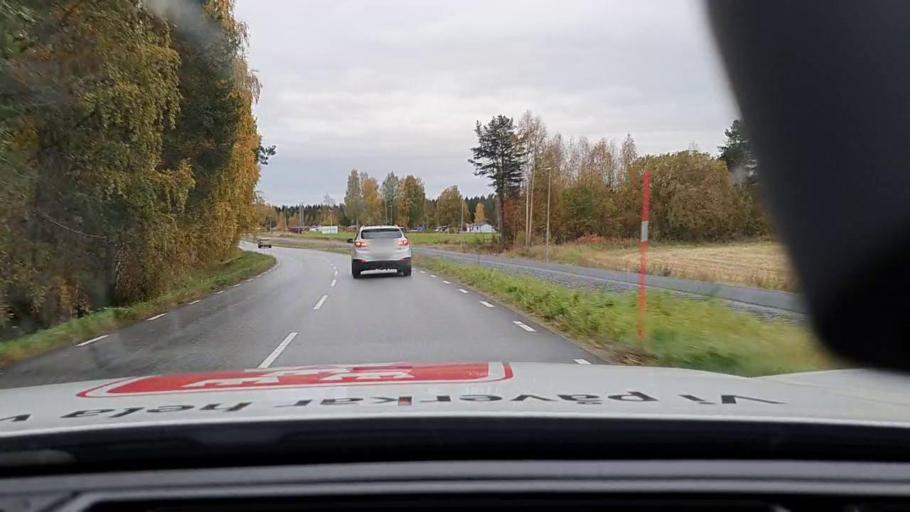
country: SE
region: Norrbotten
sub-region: Bodens Kommun
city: Saevast
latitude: 65.7689
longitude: 21.7073
